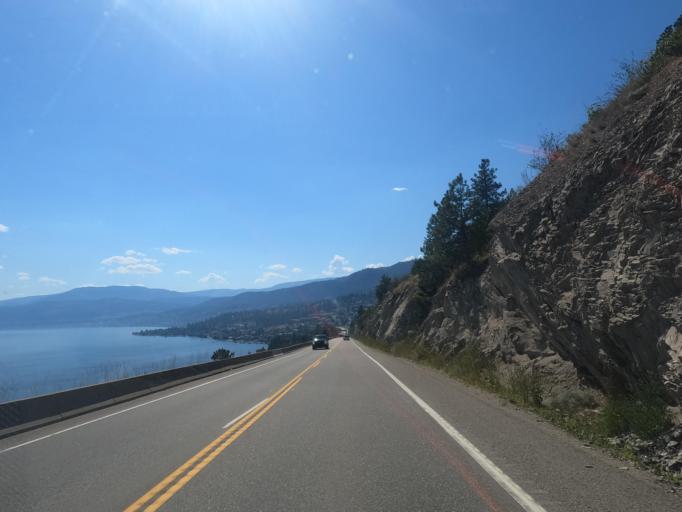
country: CA
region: British Columbia
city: Peachland
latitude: 49.7982
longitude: -119.6843
